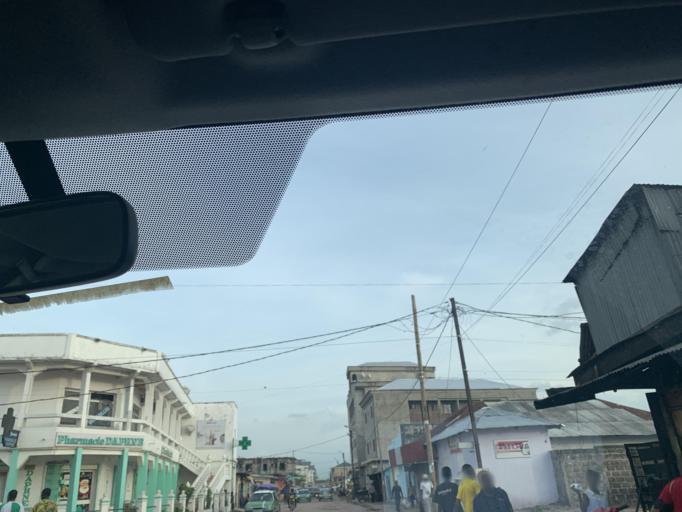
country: CG
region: Brazzaville
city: Brazzaville
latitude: -4.2540
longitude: 15.2872
